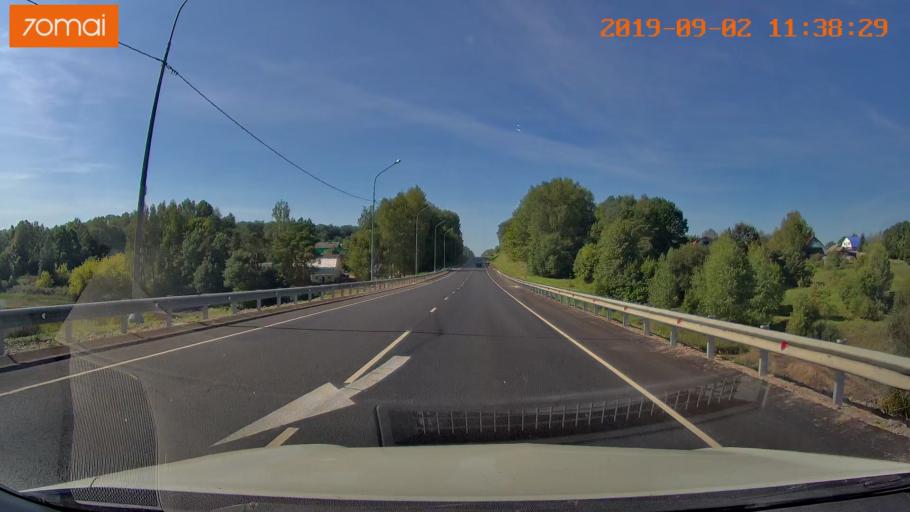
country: RU
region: Smolensk
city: Oster
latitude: 53.9130
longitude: 32.7396
